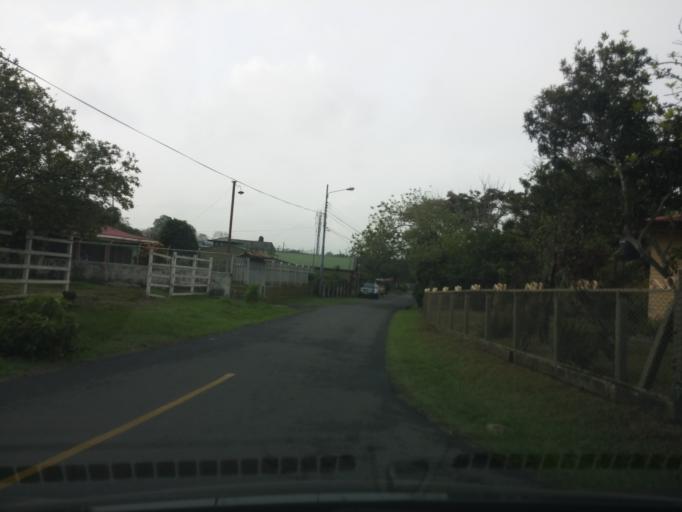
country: CR
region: Heredia
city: Llorente
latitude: 10.0093
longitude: -84.1481
